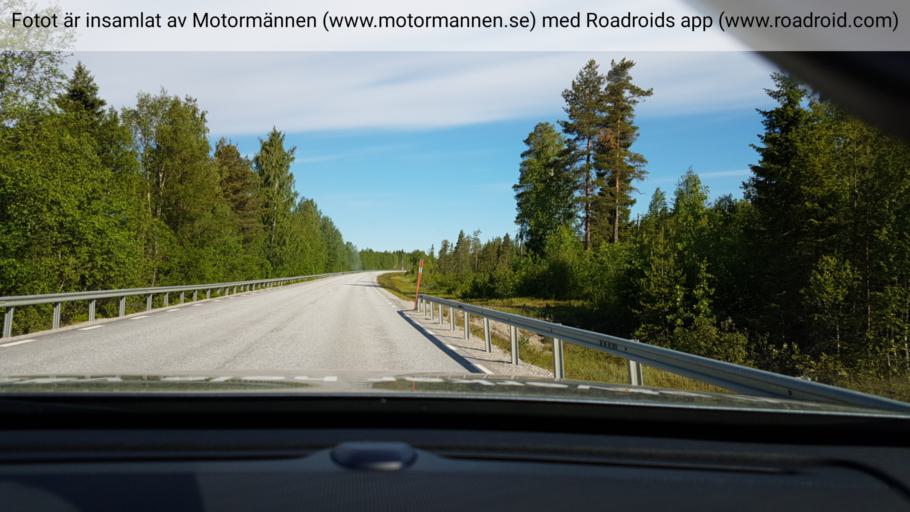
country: SE
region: Vaesterbotten
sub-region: Vindelns Kommun
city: Vindeln
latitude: 64.1867
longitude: 19.4682
